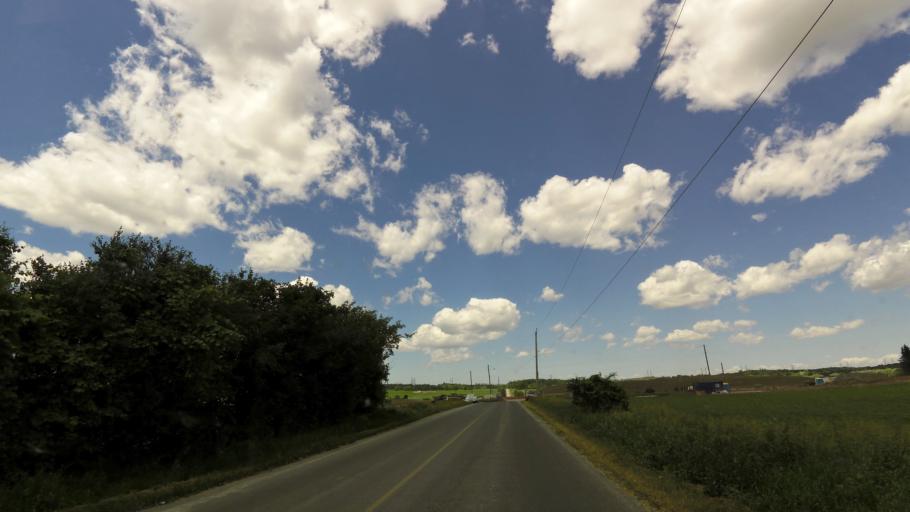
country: CA
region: Ontario
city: Oshawa
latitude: 43.9636
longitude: -78.8224
